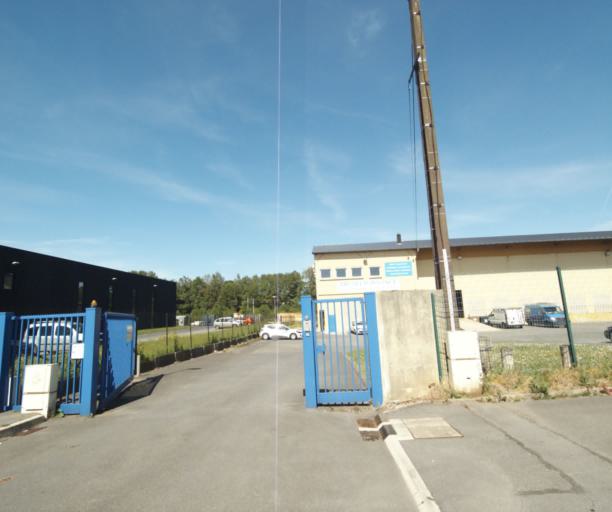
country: FR
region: Champagne-Ardenne
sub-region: Departement des Ardennes
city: Villers-Semeuse
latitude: 49.7372
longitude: 4.7316
